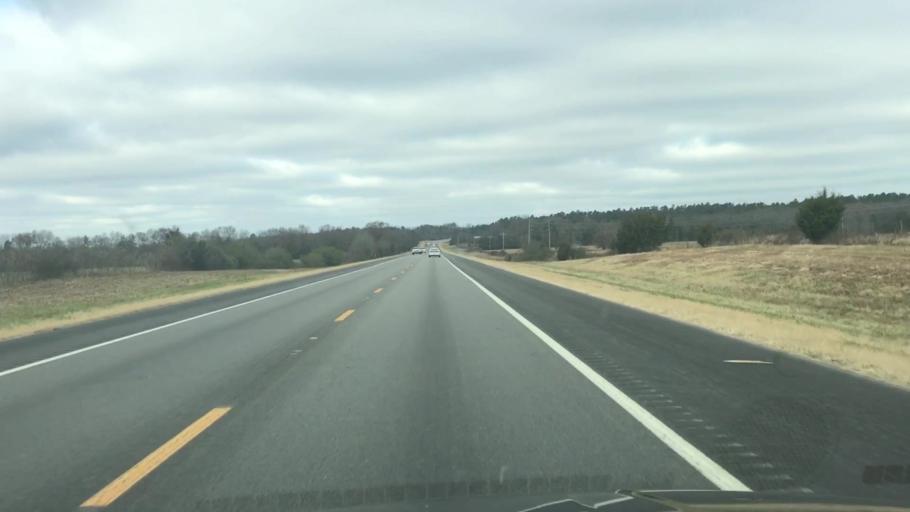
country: US
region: Arkansas
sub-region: Scott County
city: Waldron
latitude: 34.8770
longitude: -94.0948
